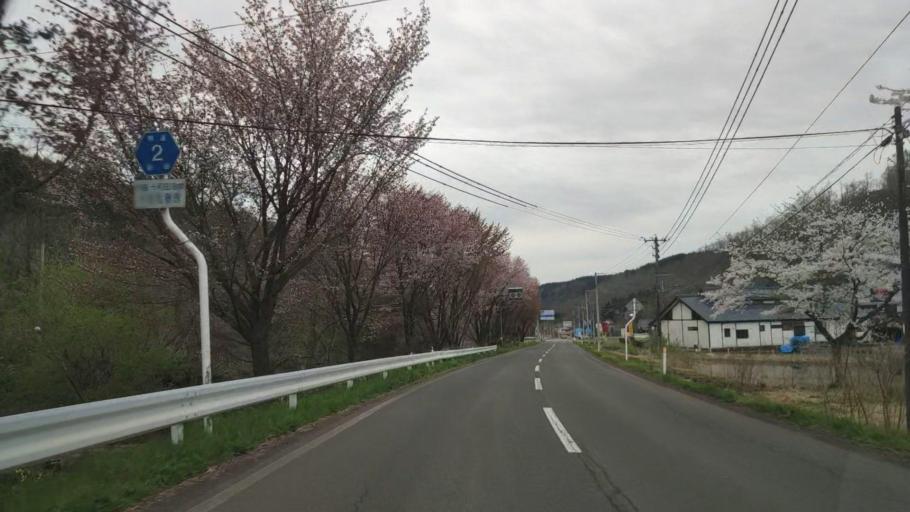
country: JP
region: Akita
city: Hanawa
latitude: 40.3584
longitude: 140.7850
